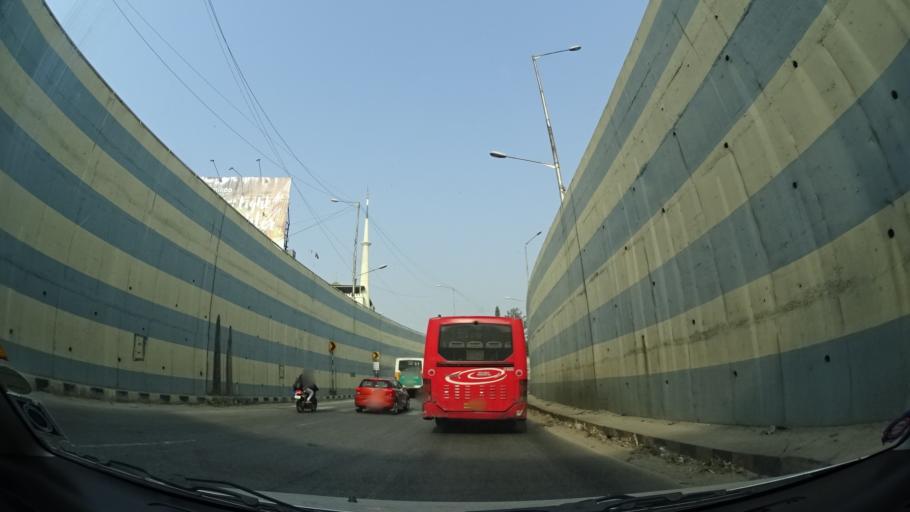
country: IN
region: Karnataka
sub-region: Bangalore Urban
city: Bangalore
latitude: 13.0275
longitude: 77.6328
